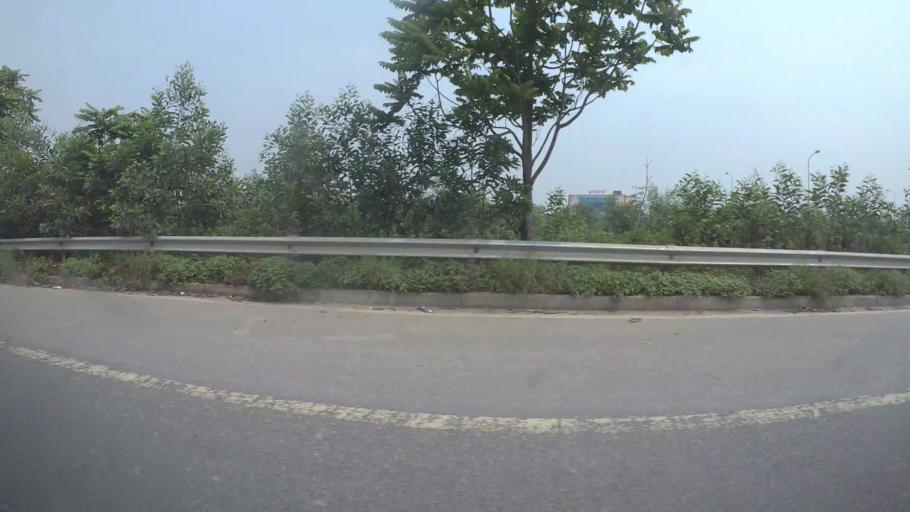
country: VN
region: Ha Noi
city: Quoc Oai
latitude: 21.0026
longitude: 105.6519
